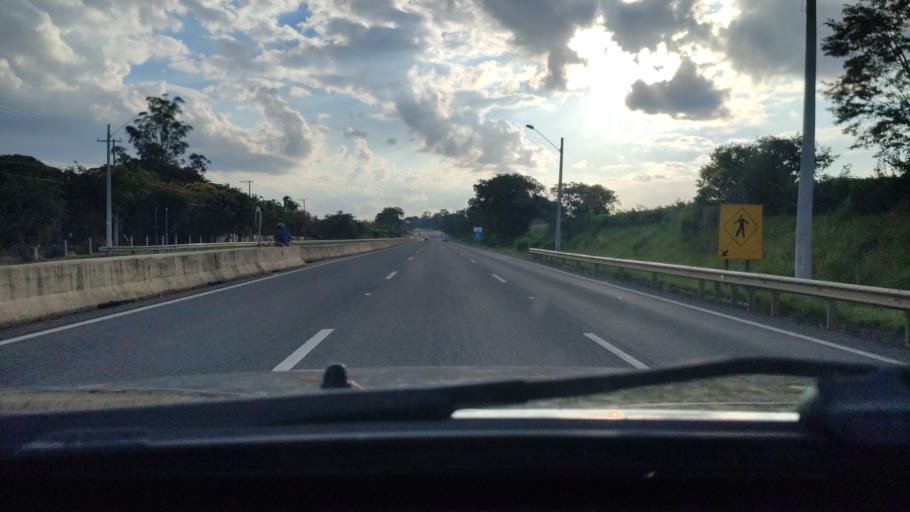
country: BR
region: Sao Paulo
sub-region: Mogi-Mirim
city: Mogi Mirim
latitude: -22.4504
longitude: -47.0740
